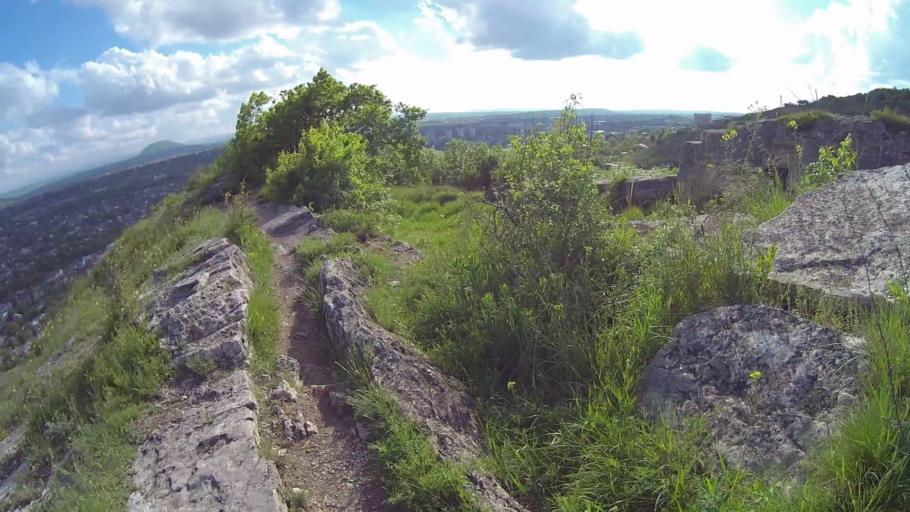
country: RU
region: Stavropol'skiy
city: Goryachevodskiy
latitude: 44.0384
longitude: 43.0883
